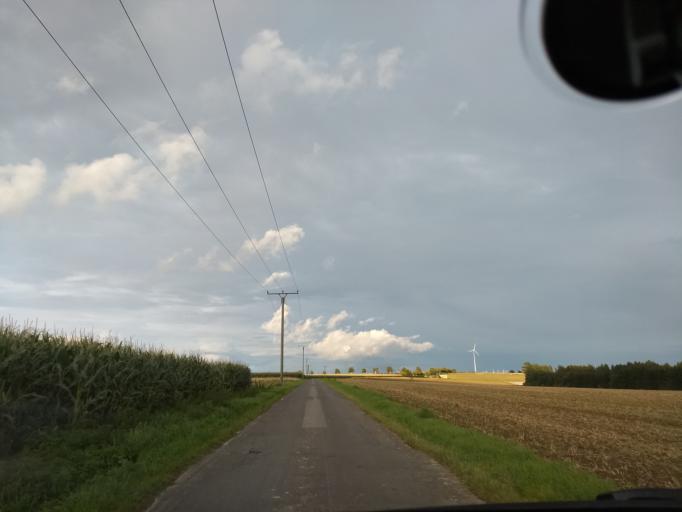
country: DE
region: North Rhine-Westphalia
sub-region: Regierungsbezirk Arnsberg
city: Ruthen
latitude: 51.4974
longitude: 8.4612
